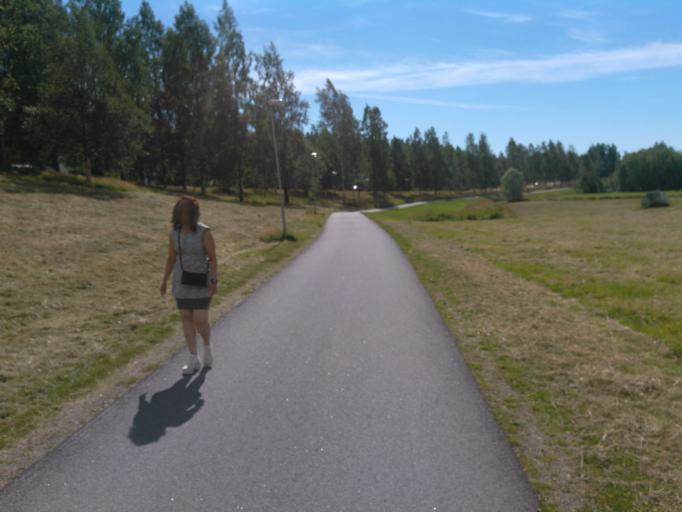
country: SE
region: Vaesterbotten
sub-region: Umea Kommun
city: Ersmark
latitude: 63.8396
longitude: 20.3168
